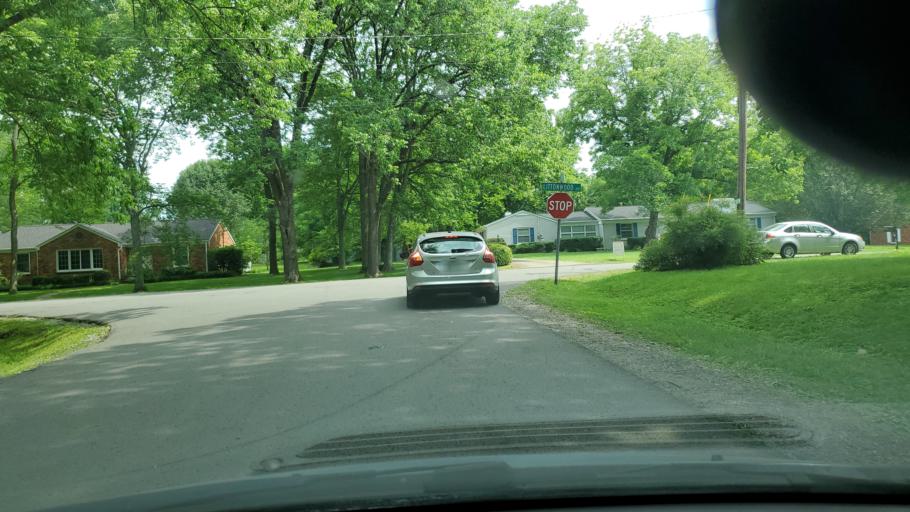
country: US
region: Tennessee
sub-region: Davidson County
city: Lakewood
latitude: 36.2272
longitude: -86.7200
